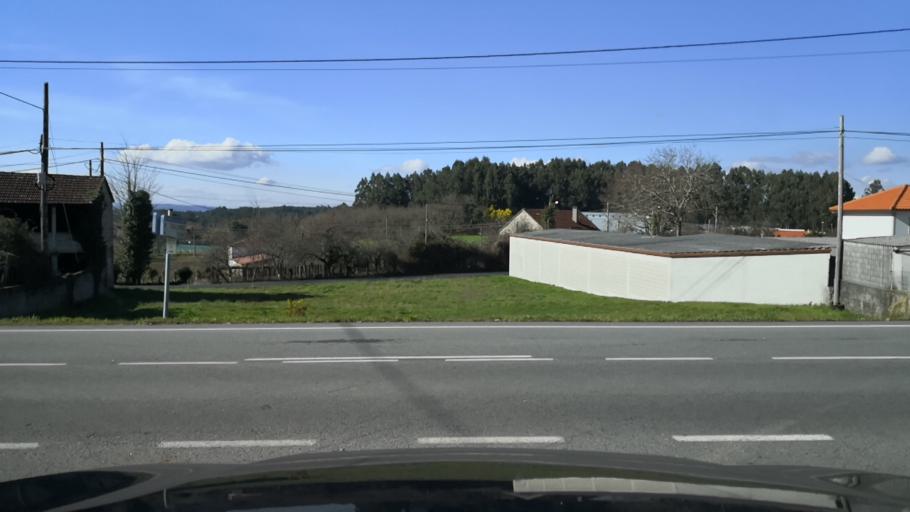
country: ES
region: Galicia
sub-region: Provincia da Coruna
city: Ribeira
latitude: 42.7184
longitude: -8.4419
